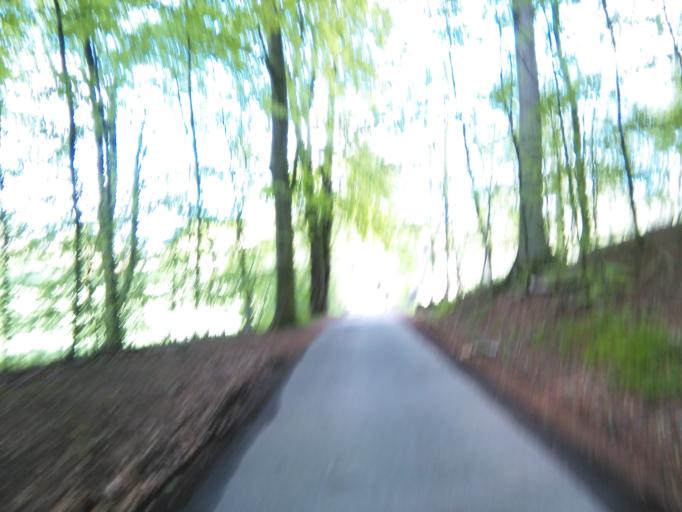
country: DK
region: Central Jutland
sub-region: Arhus Kommune
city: Beder
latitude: 56.0854
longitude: 10.2336
